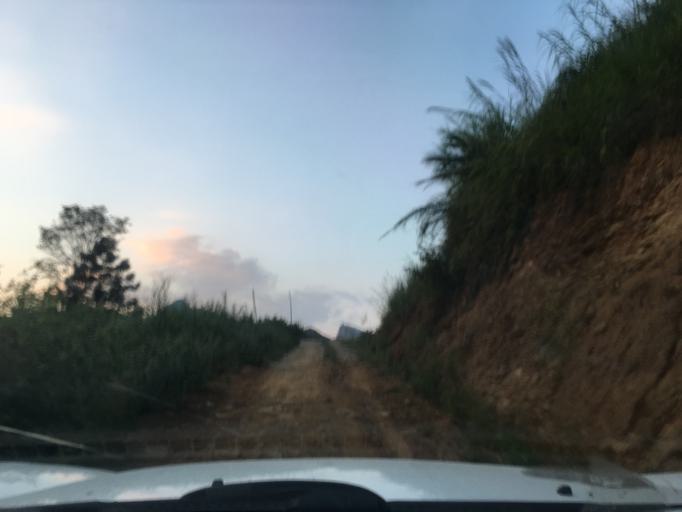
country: CN
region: Guangxi Zhuangzu Zizhiqu
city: Xinzhou
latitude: 25.3479
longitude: 105.7386
